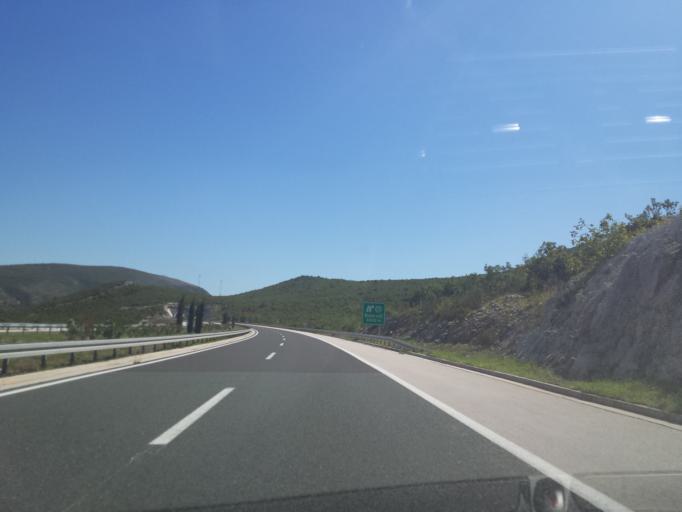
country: HR
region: Splitsko-Dalmatinska
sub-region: Grad Omis
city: Omis
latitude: 43.4791
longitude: 16.8119
